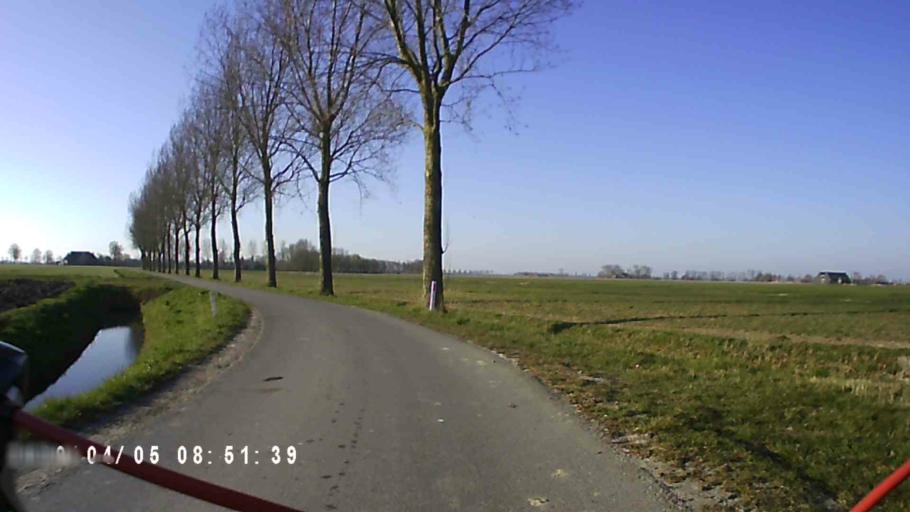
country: NL
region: Groningen
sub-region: Gemeente Zuidhorn
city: Aduard
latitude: 53.3130
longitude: 6.4644
